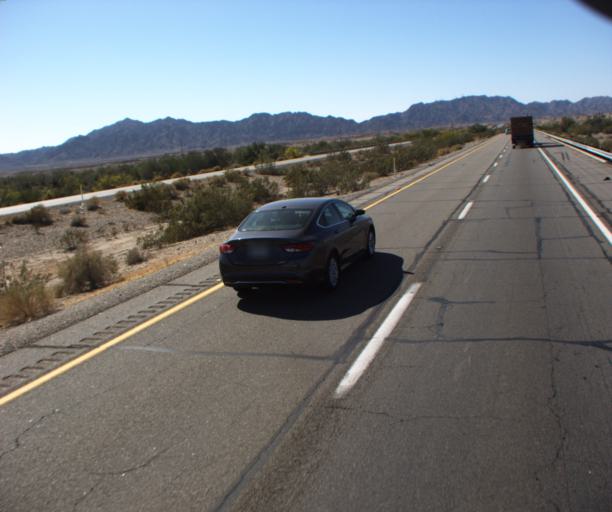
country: US
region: Arizona
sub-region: Yuma County
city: Wellton
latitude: 32.6585
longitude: -114.2482
